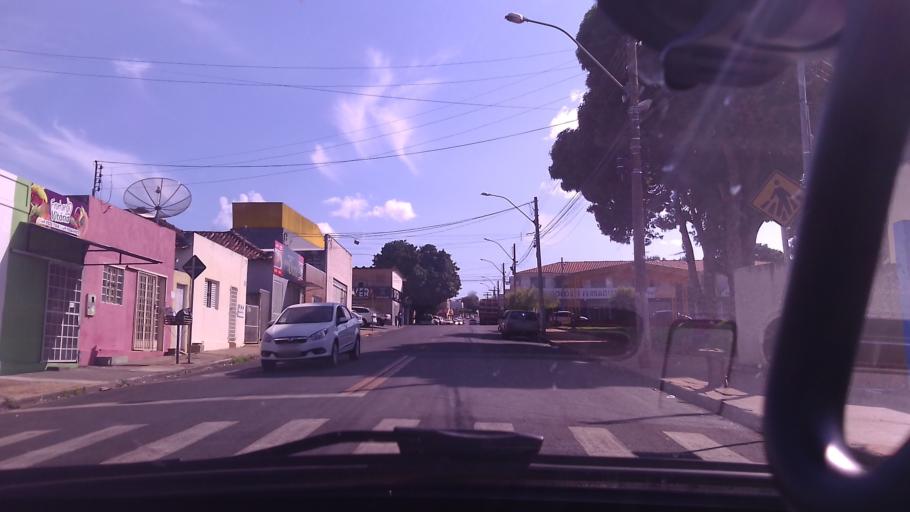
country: BR
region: Goias
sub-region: Mineiros
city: Mineiros
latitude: -17.5647
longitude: -52.5500
